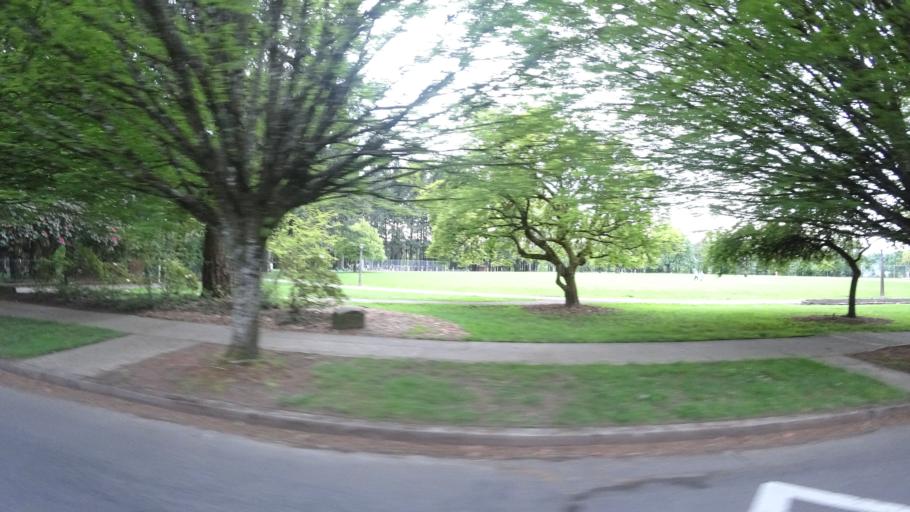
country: US
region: Oregon
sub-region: Clackamas County
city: Milwaukie
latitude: 45.4680
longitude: -122.6591
